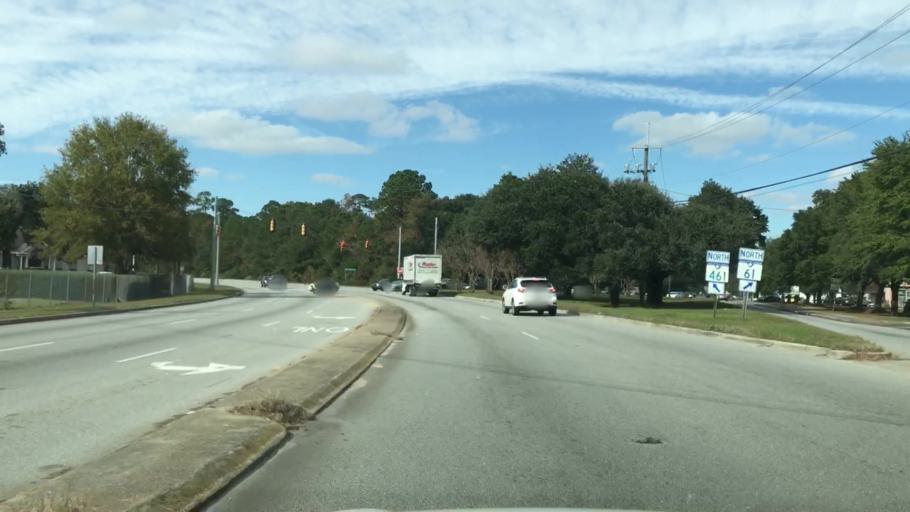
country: US
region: South Carolina
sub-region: Charleston County
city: North Charleston
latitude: 32.8071
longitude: -80.0232
